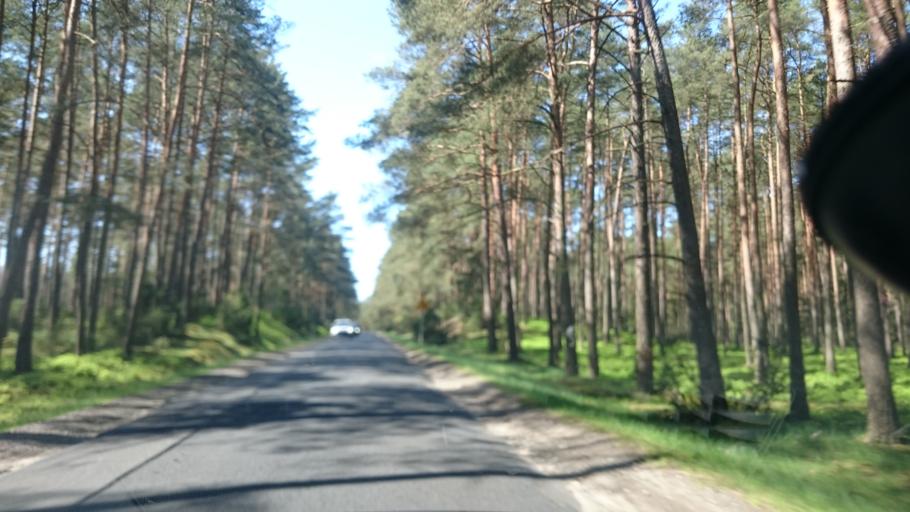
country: PL
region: Kujawsko-Pomorskie
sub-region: Powiat swiecki
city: Jezewo
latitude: 53.6136
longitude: 18.5272
